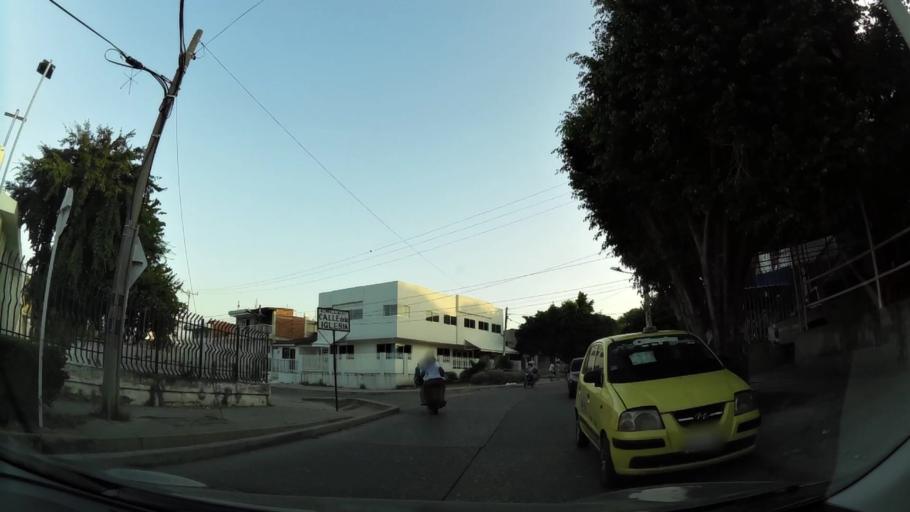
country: CO
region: Bolivar
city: Cartagena
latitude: 10.3877
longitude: -75.4871
